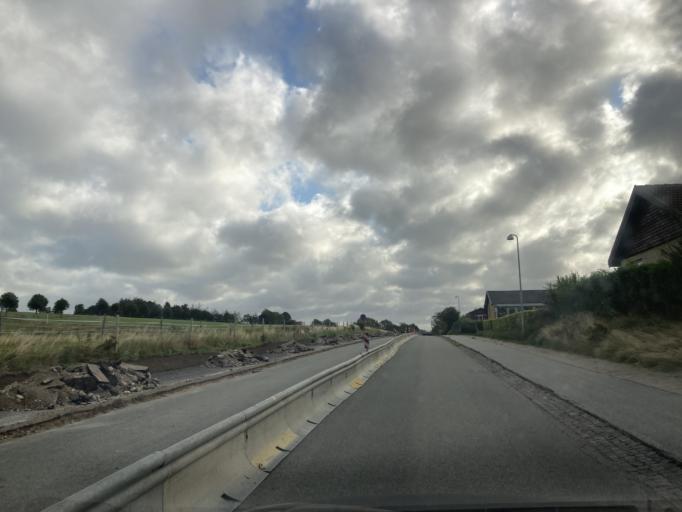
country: DK
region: Capital Region
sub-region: Halsnaes Kommune
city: Frederiksvaerk
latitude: 55.9543
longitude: 12.0324
